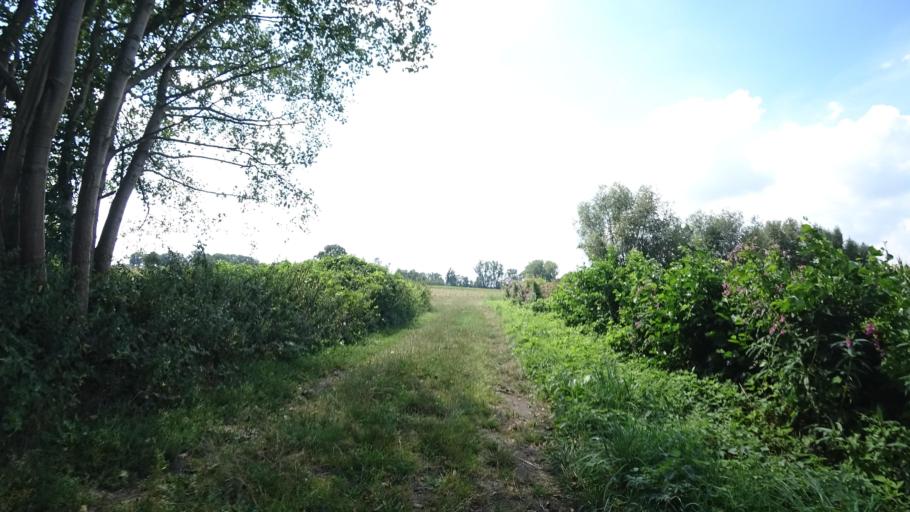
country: DE
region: North Rhine-Westphalia
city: Rietberg
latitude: 51.8689
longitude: 8.4428
